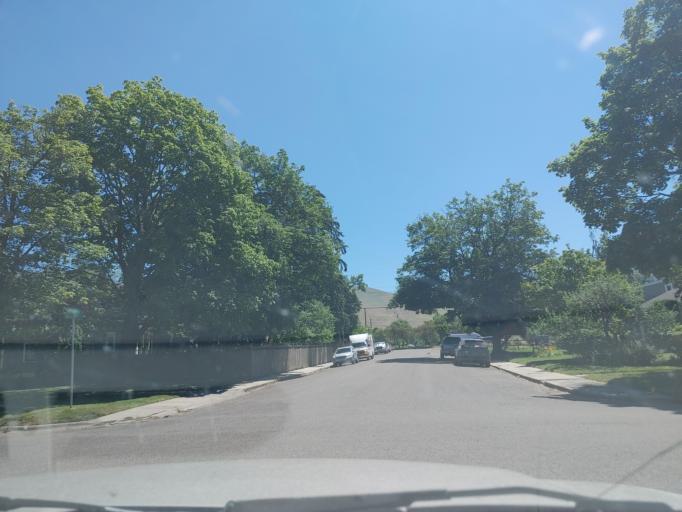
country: US
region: Montana
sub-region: Missoula County
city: Missoula
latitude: 46.8617
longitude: -114.0081
